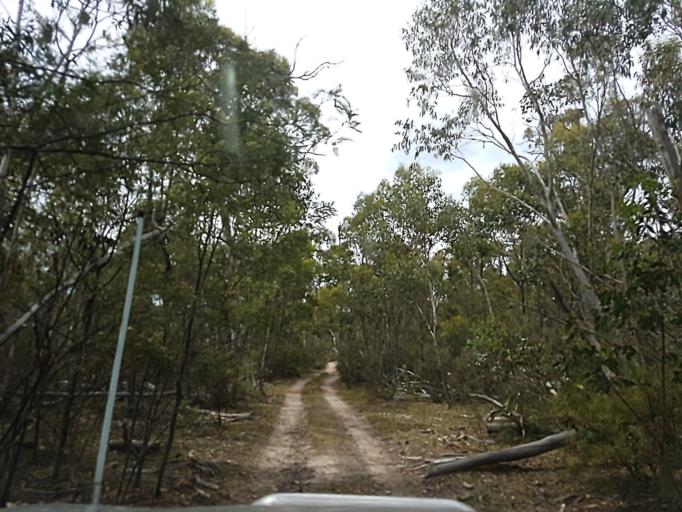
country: AU
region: New South Wales
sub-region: Snowy River
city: Jindabyne
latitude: -36.8286
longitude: 148.2236
